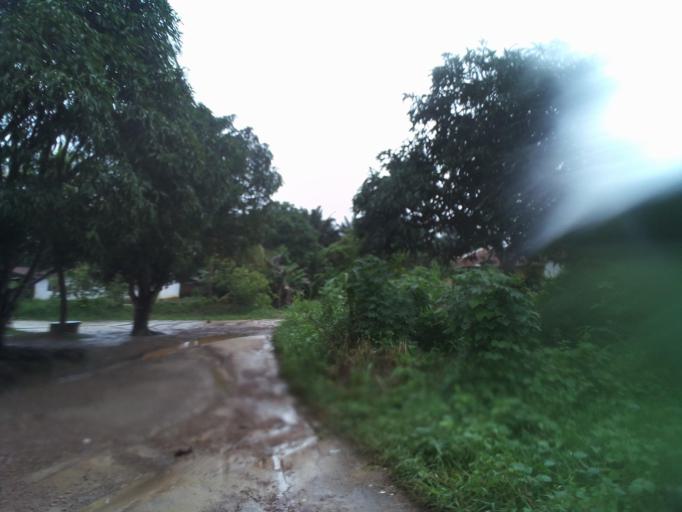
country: SL
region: Eastern Province
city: Kenema
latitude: 7.8512
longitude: -11.1970
